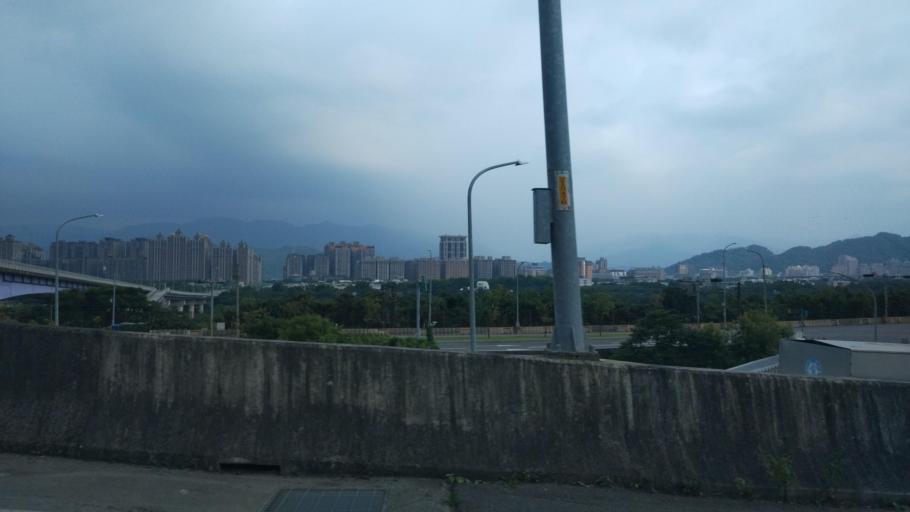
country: TW
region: Taiwan
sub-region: Taoyuan
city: Taoyuan
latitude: 24.9592
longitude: 121.3711
